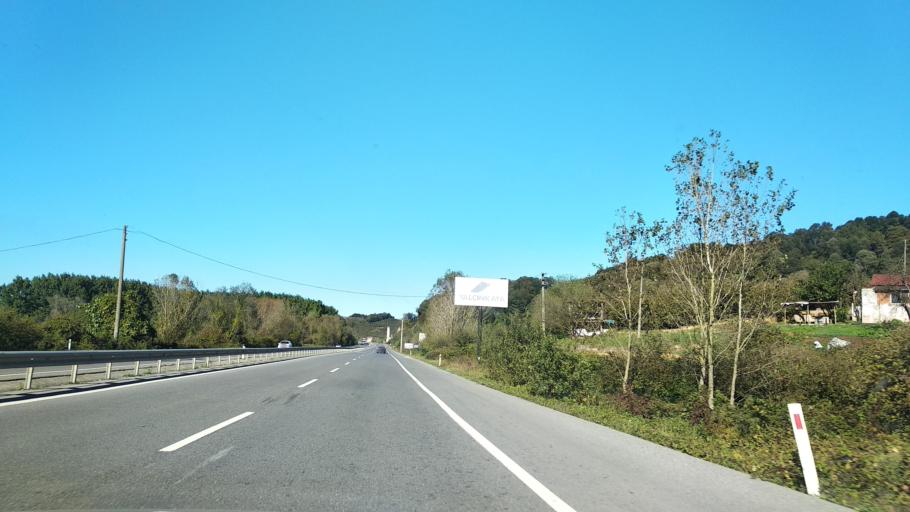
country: TR
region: Sakarya
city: Karasu
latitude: 41.0679
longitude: 30.6438
